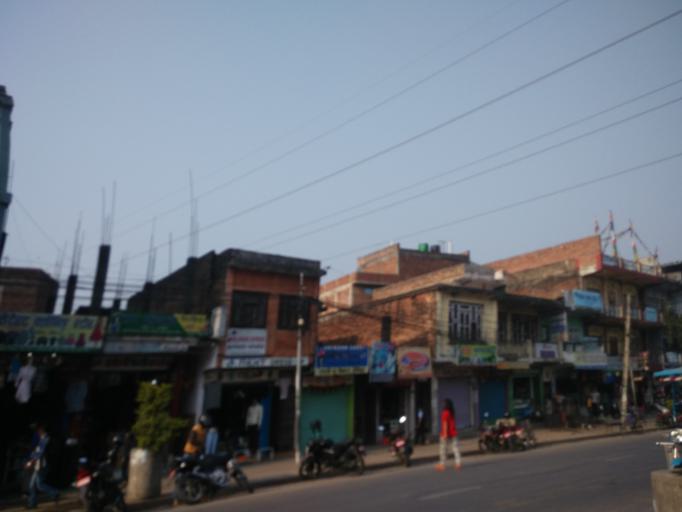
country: NP
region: Central Region
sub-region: Narayani Zone
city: Hitura
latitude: 27.4313
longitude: 85.0309
